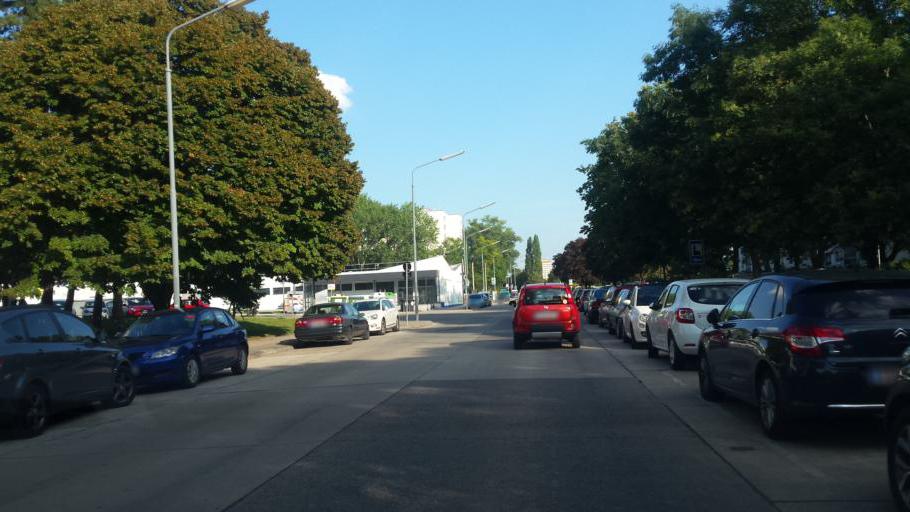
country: AT
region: Lower Austria
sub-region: Politischer Bezirk Wien-Umgebung
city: Leopoldsdorf
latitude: 48.1460
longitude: 16.3899
